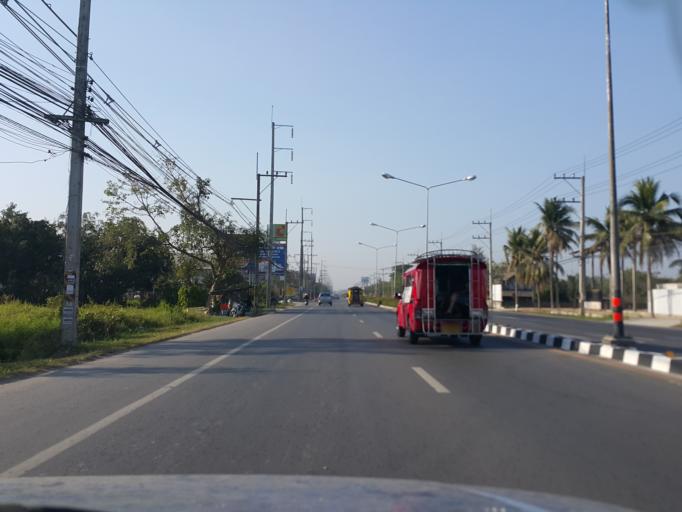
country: TH
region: Chiang Mai
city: Hang Dong
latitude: 18.6703
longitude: 98.9137
